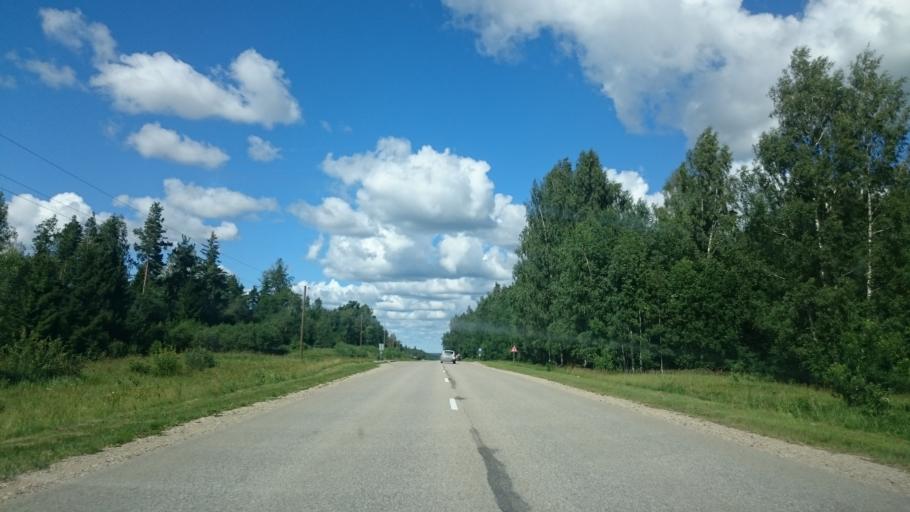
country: LV
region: Kuldigas Rajons
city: Kuldiga
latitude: 56.9375
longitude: 21.9292
